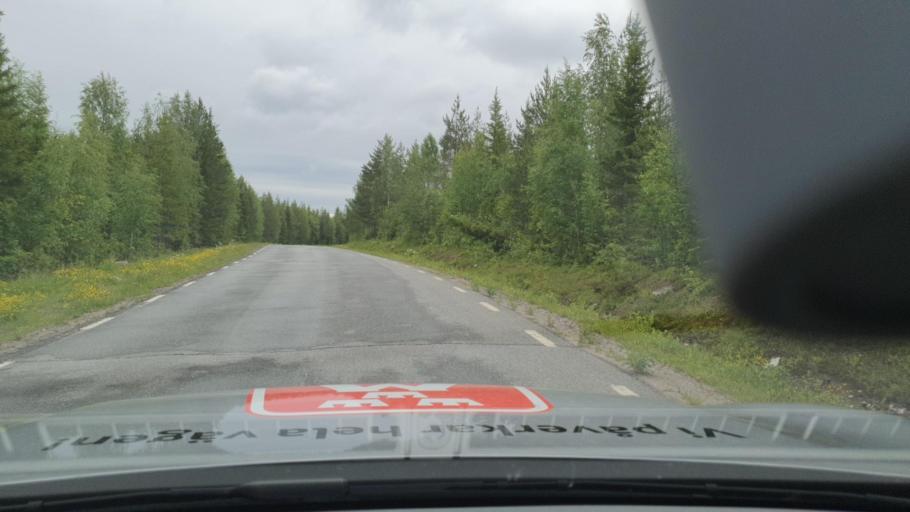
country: SE
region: Norrbotten
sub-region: Lulea Kommun
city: Ranea
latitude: 65.8055
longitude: 22.3062
